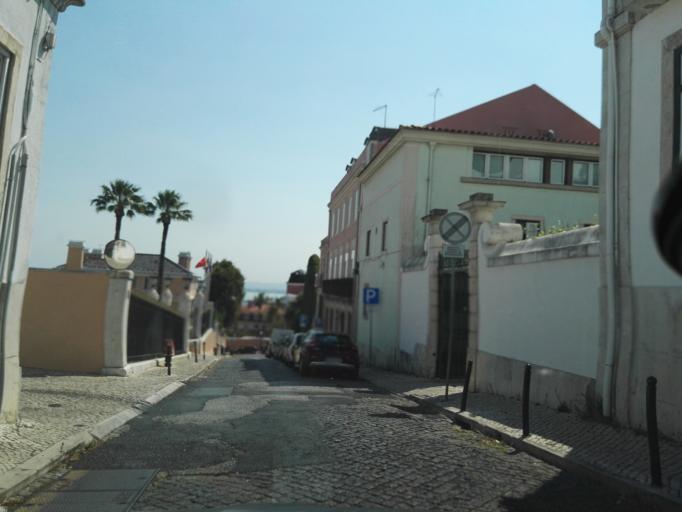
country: PT
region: Setubal
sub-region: Almada
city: Cacilhas
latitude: 38.7070
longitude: -9.1642
